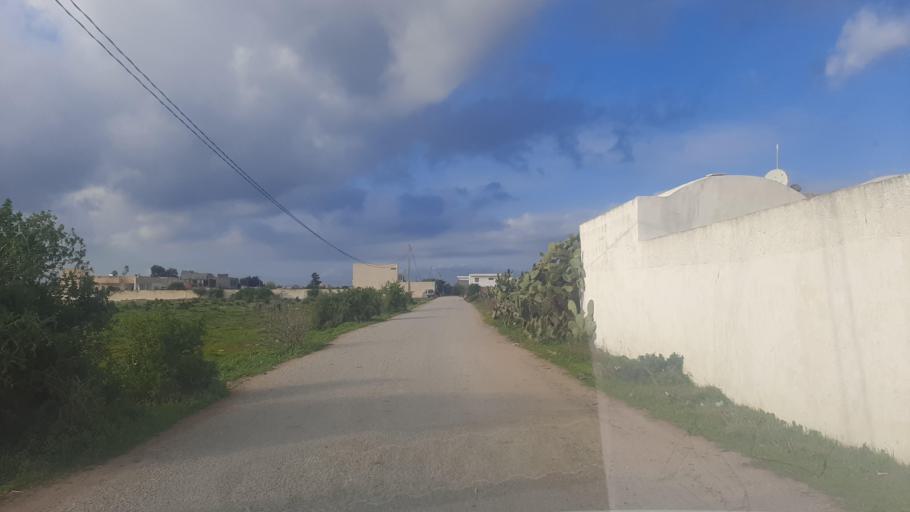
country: TN
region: Nabul
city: Manzil Bu Zalafah
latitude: 36.7147
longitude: 10.4976
